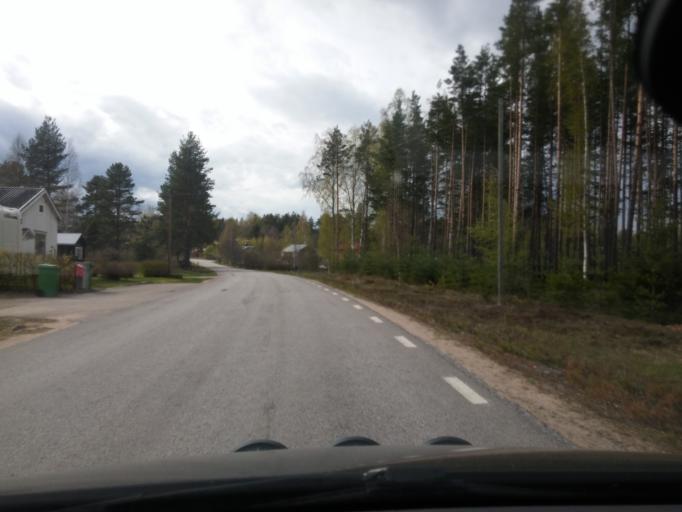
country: SE
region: Gaevleborg
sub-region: Ljusdals Kommun
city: Farila
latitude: 61.8001
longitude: 15.9047
